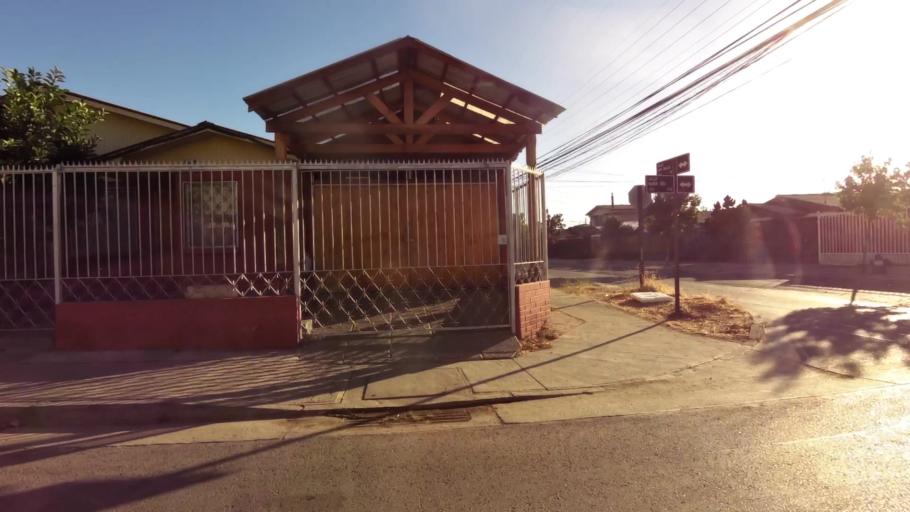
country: CL
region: O'Higgins
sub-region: Provincia de Cachapoal
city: Rancagua
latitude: -34.1766
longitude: -70.7633
